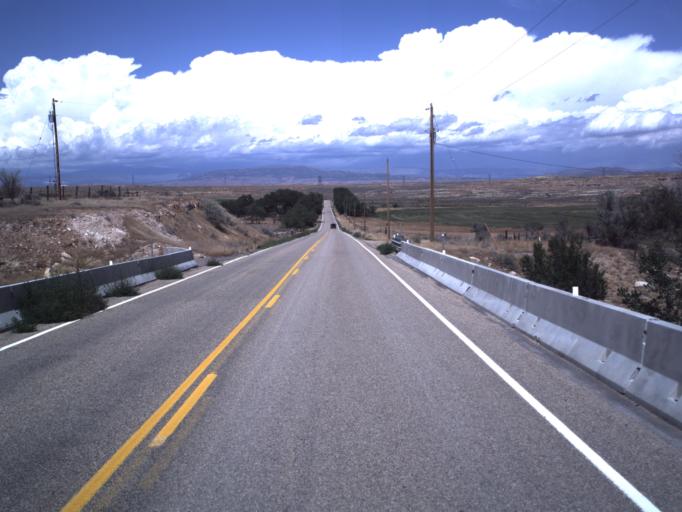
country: US
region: Utah
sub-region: Uintah County
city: Maeser
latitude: 40.2455
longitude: -109.6843
